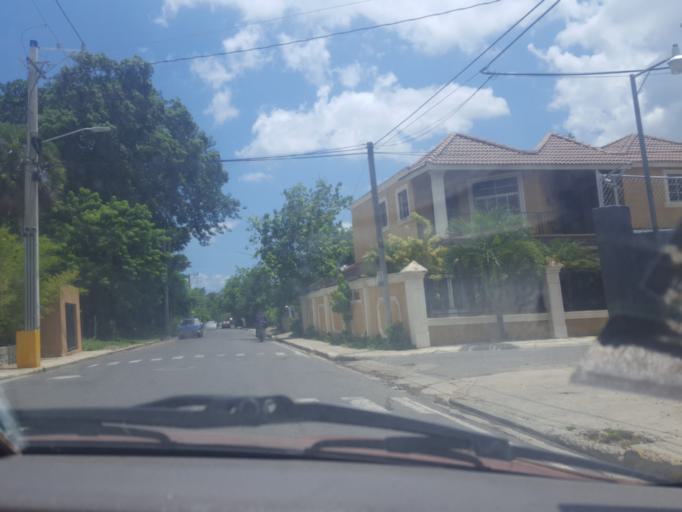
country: DO
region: Santiago
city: Tamboril
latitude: 19.4813
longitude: -70.6577
